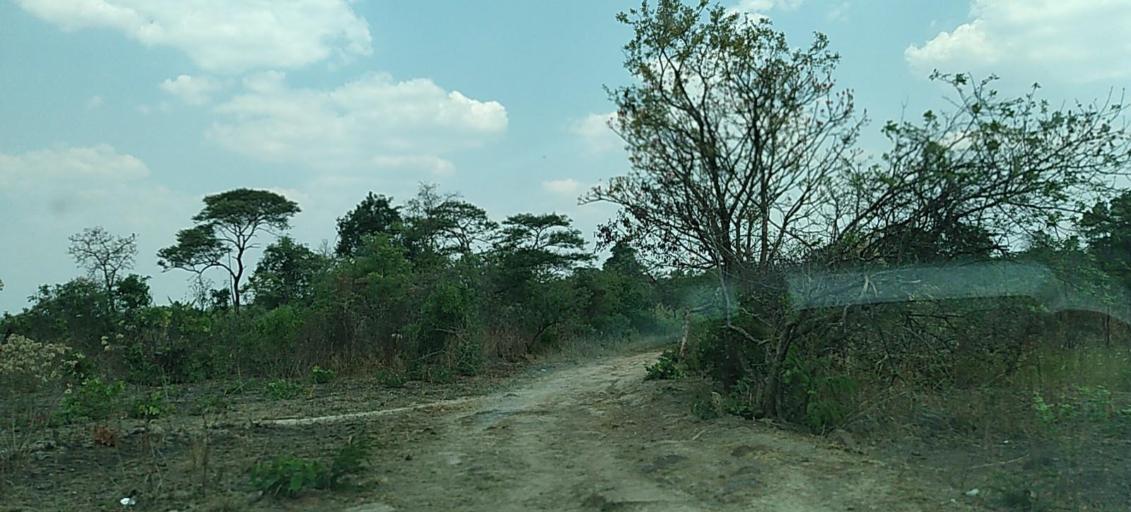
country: CD
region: Katanga
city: Kipushi
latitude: -11.9936
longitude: 27.4182
